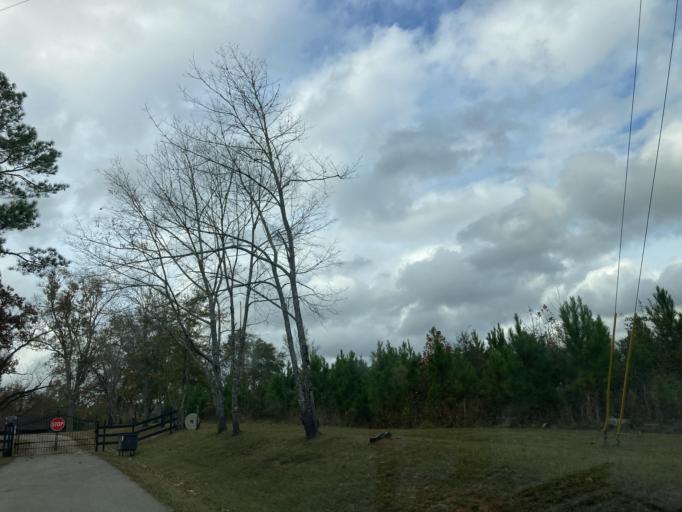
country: US
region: Mississippi
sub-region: Lamar County
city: Purvis
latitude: 31.1867
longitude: -89.5788
